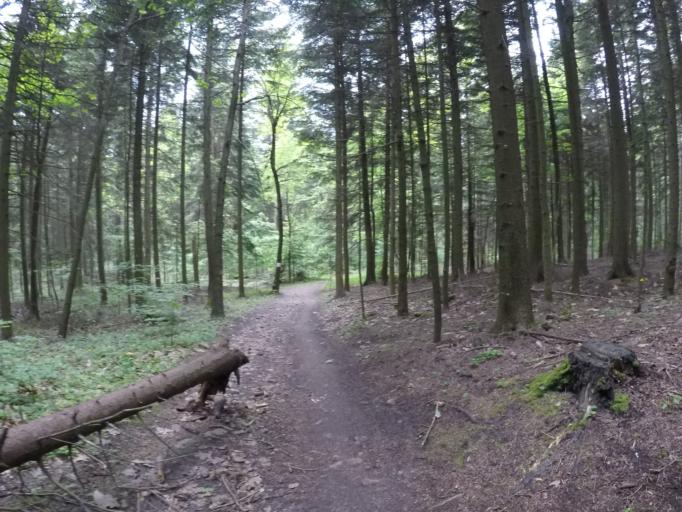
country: PL
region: Swietokrzyskie
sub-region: Powiat kielecki
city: Kielce
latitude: 50.8366
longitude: 20.6008
